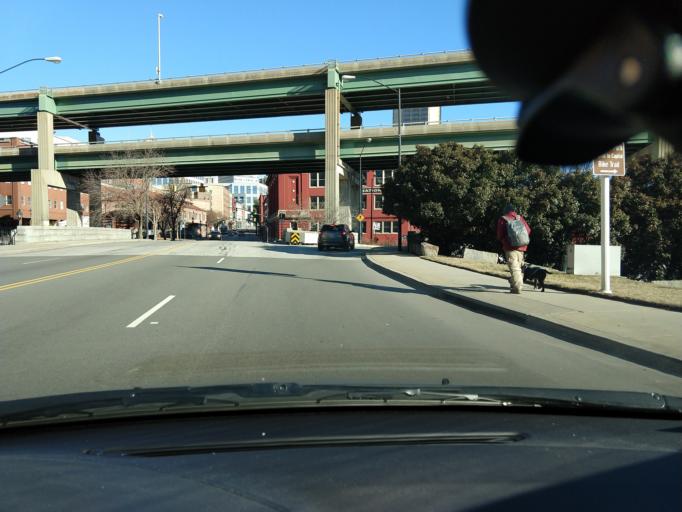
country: US
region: Virginia
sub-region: City of Richmond
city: Richmond
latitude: 37.5326
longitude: -77.4329
